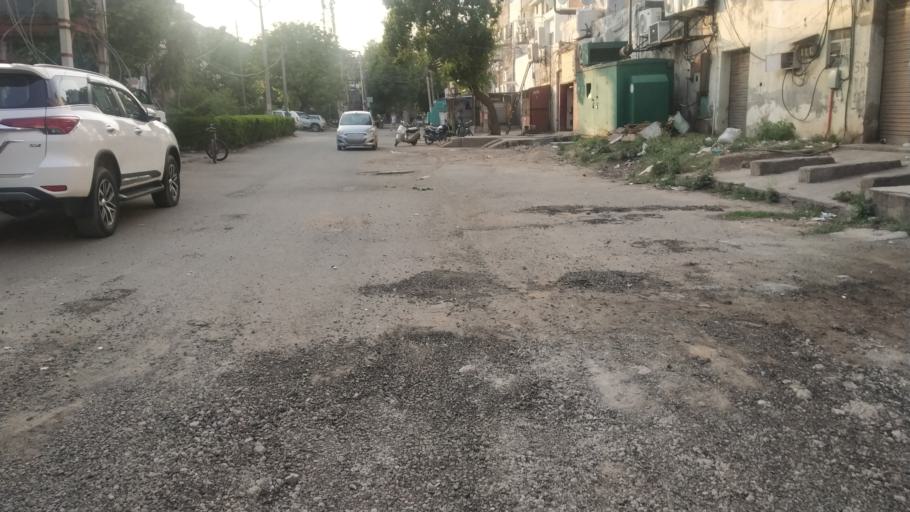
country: IN
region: Punjab
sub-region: Ajitgarh
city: Mohali
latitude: 30.7084
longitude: 76.7227
